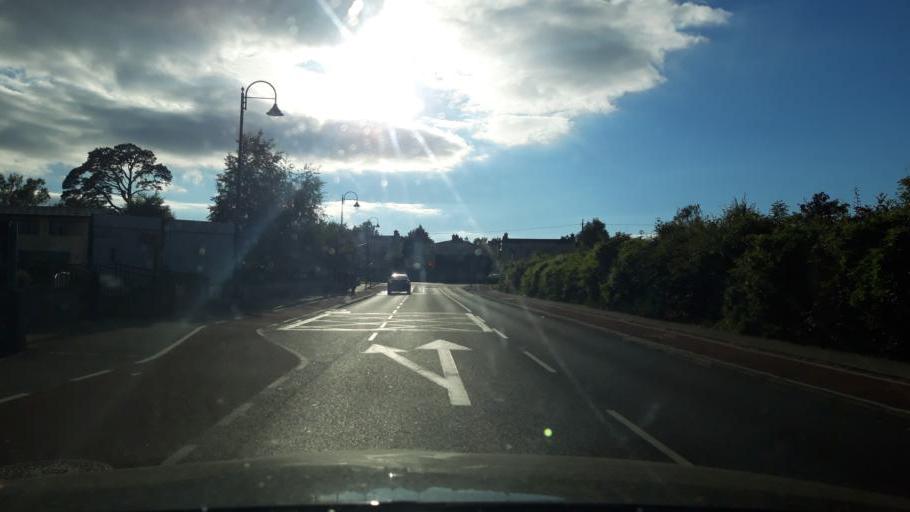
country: IE
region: Leinster
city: Little Bray
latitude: 53.1893
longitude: -6.1242
